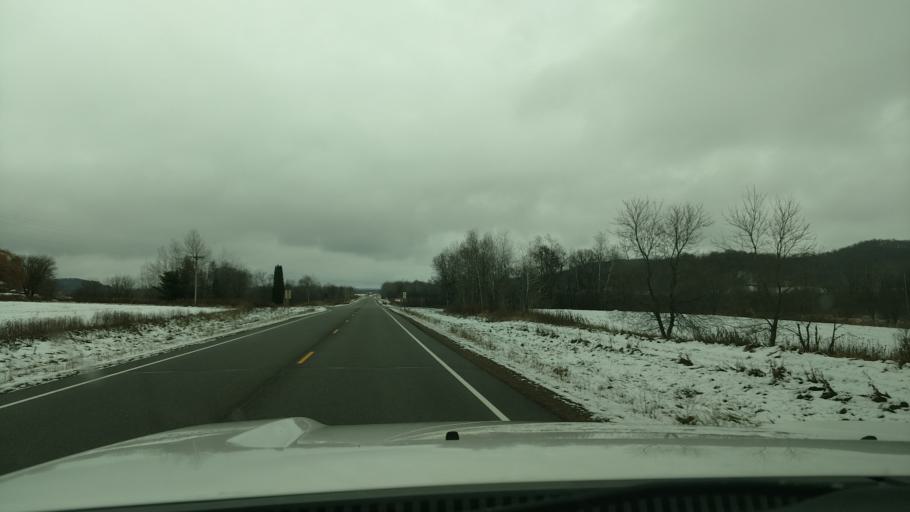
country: US
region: Wisconsin
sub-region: Dunn County
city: Colfax
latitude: 45.1374
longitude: -91.7911
